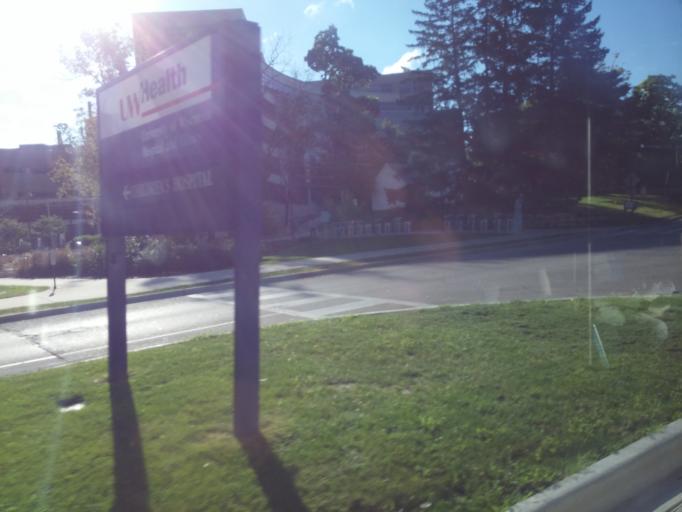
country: US
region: Wisconsin
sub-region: Dane County
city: Shorewood Hills
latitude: 43.0761
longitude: -89.4341
